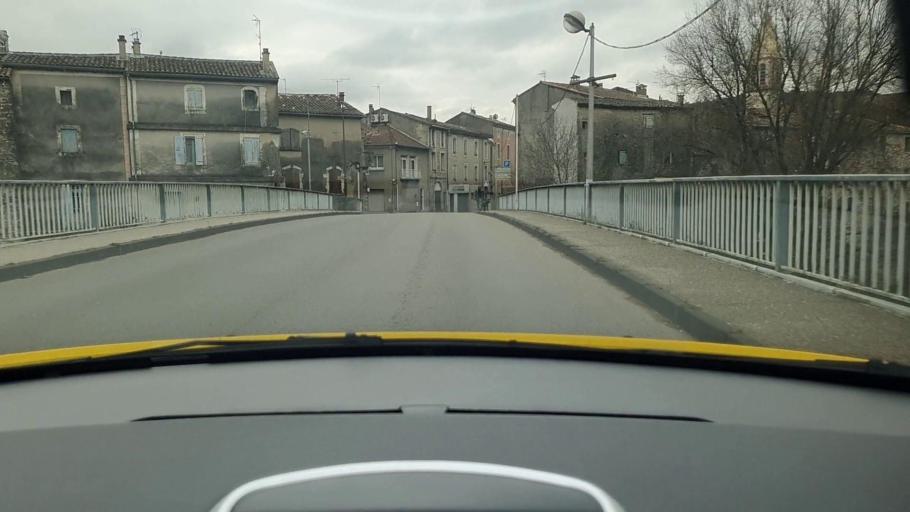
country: FR
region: Languedoc-Roussillon
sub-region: Departement du Gard
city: Saint-Ambroix
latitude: 44.2629
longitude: 4.2000
